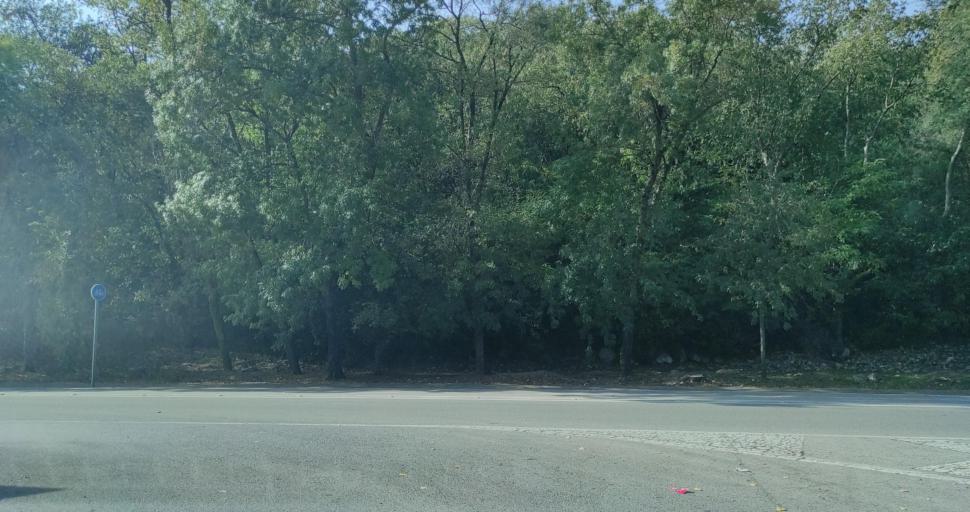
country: ES
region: Catalonia
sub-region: Provincia de Girona
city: Girona
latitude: 41.9949
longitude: 2.8192
